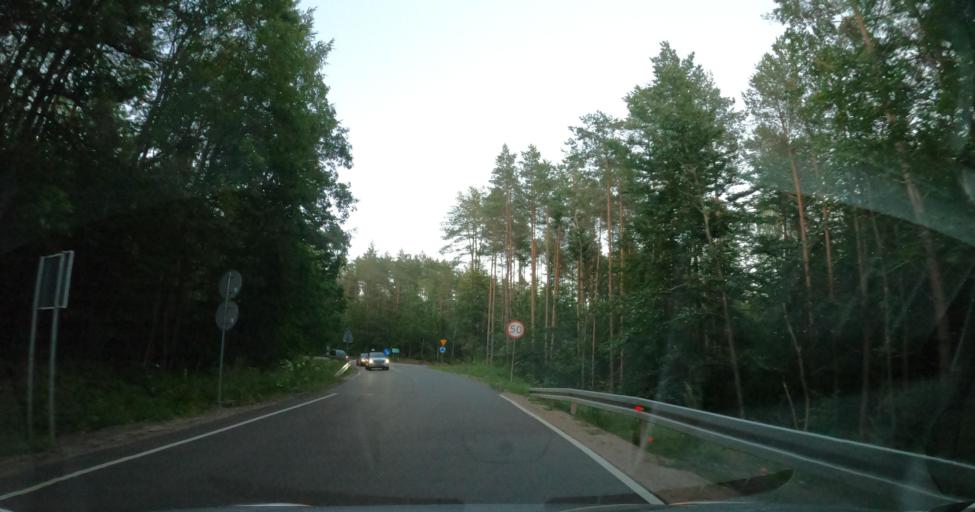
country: PL
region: Pomeranian Voivodeship
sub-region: Powiat leborski
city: Lebork
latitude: 54.5113
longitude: 17.8065
